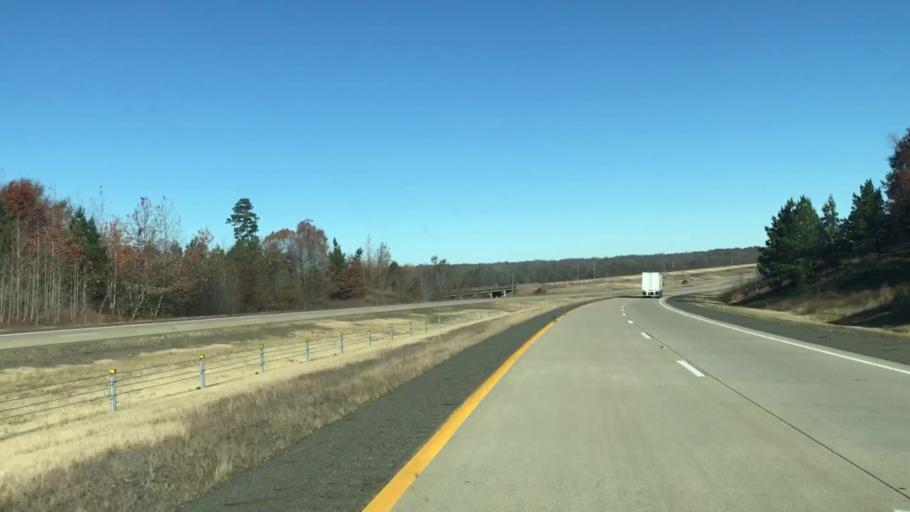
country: US
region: Texas
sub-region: Cass County
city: Queen City
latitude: 33.1334
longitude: -93.8944
